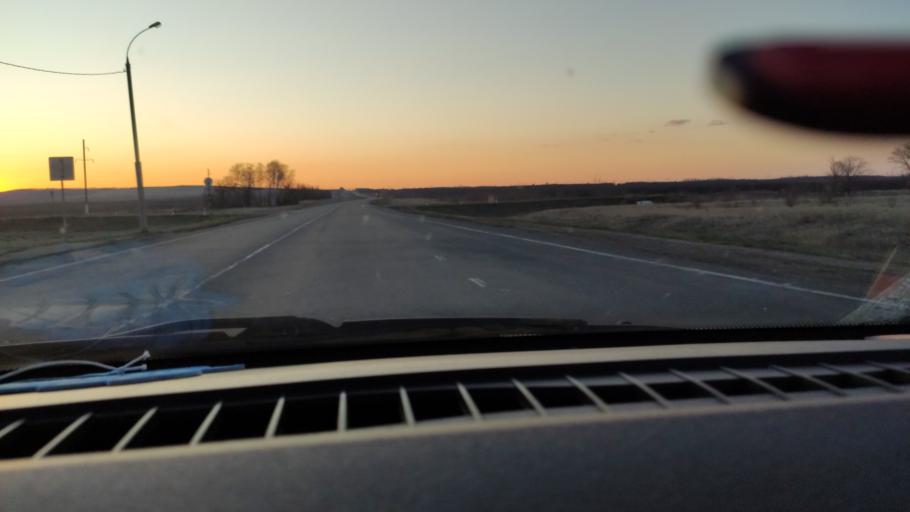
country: RU
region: Saratov
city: Yelshanka
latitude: 51.8305
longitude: 46.2381
